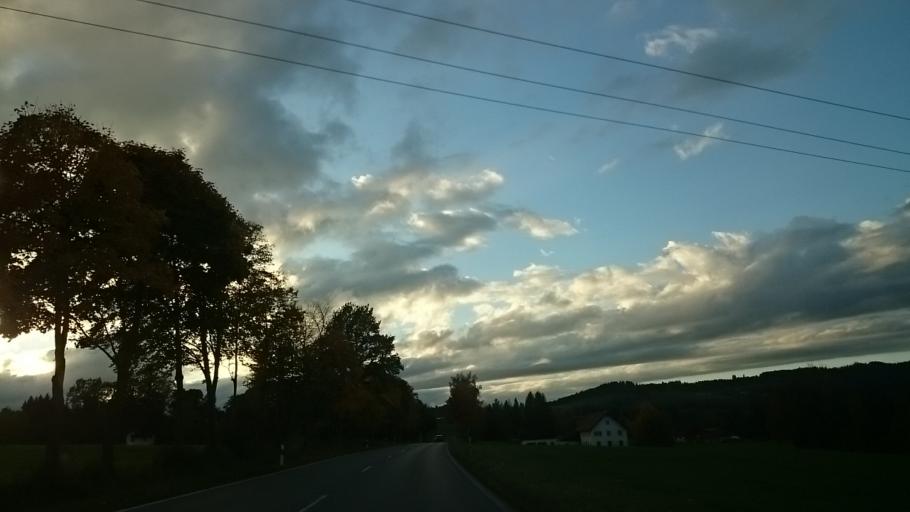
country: DE
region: Bavaria
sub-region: Upper Bavaria
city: Rottenbuch
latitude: 47.7334
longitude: 10.9554
